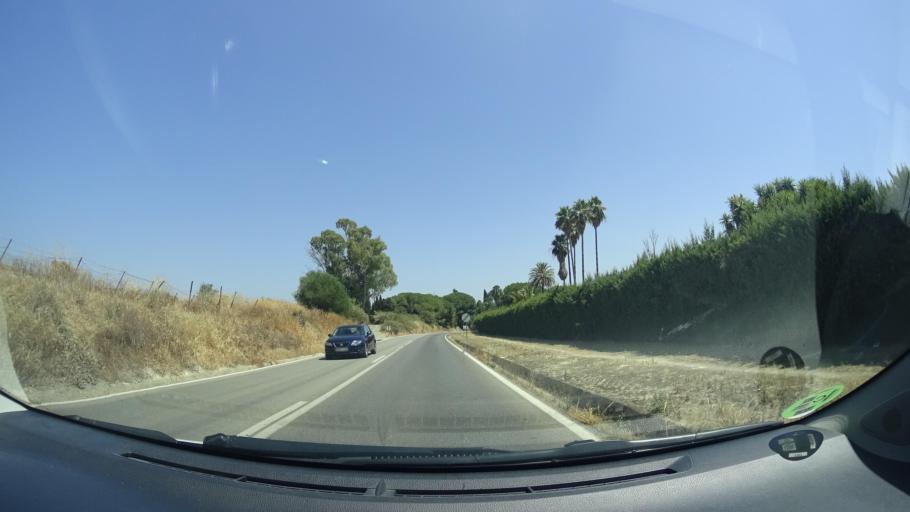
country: ES
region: Andalusia
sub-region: Provincia de Cadiz
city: Jerez de la Frontera
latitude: 36.6638
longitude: -6.1105
